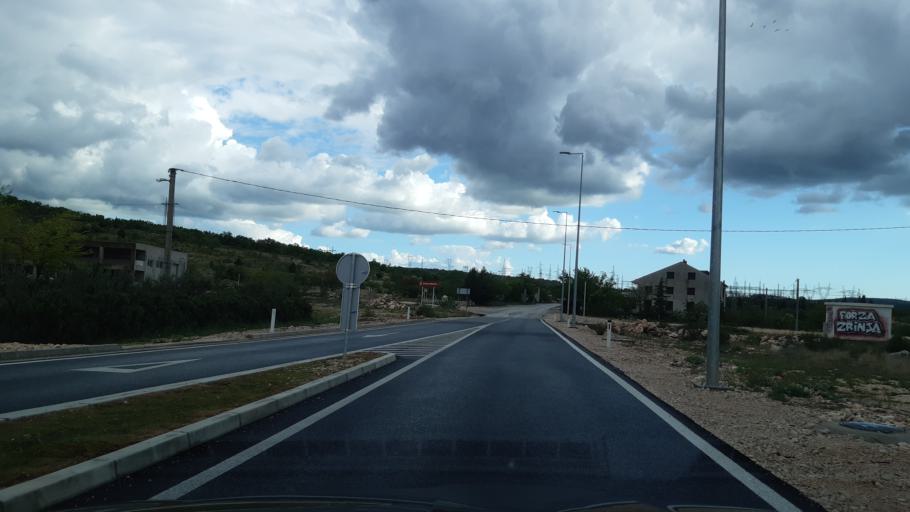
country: BA
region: Federation of Bosnia and Herzegovina
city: Rodoc
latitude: 43.3110
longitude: 17.7734
